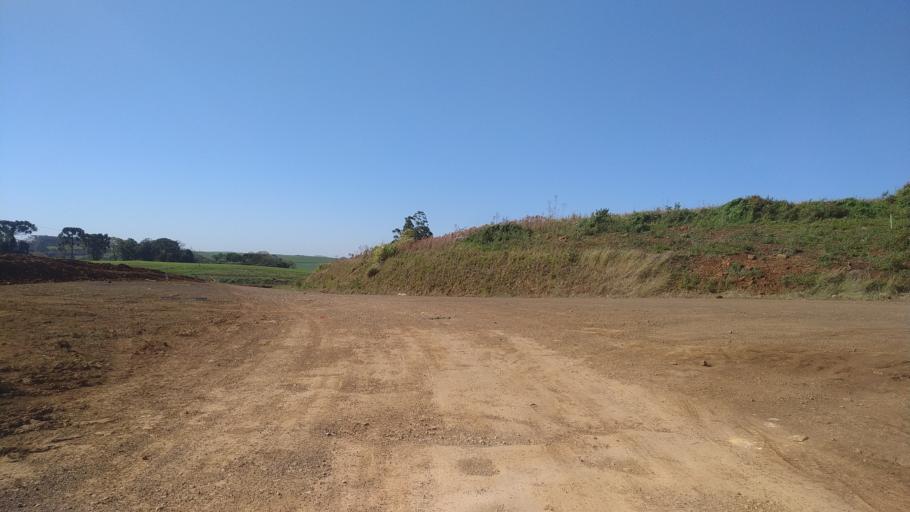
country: BR
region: Santa Catarina
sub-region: Chapeco
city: Chapeco
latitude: -27.1504
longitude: -52.6034
